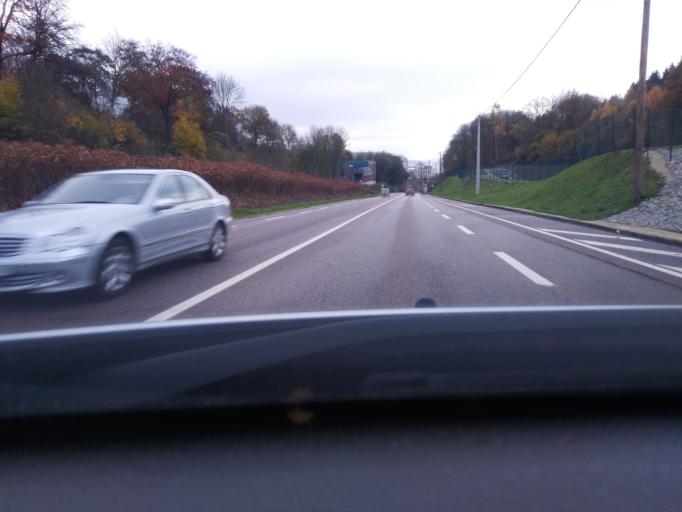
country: FR
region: Haute-Normandie
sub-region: Departement de la Seine-Maritime
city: Maromme
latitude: 49.4866
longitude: 1.0332
